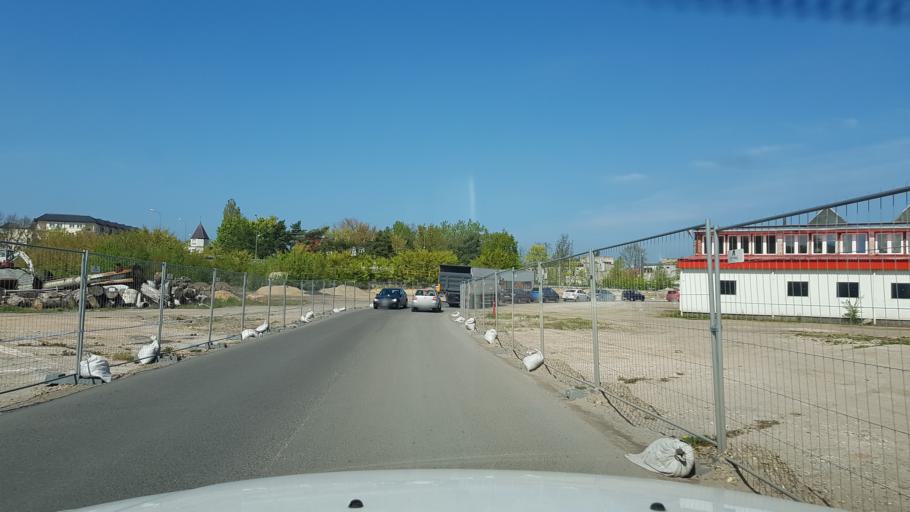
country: PL
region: Pomeranian Voivodeship
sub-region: Powiat slupski
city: Ustka
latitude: 54.5795
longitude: 16.8537
